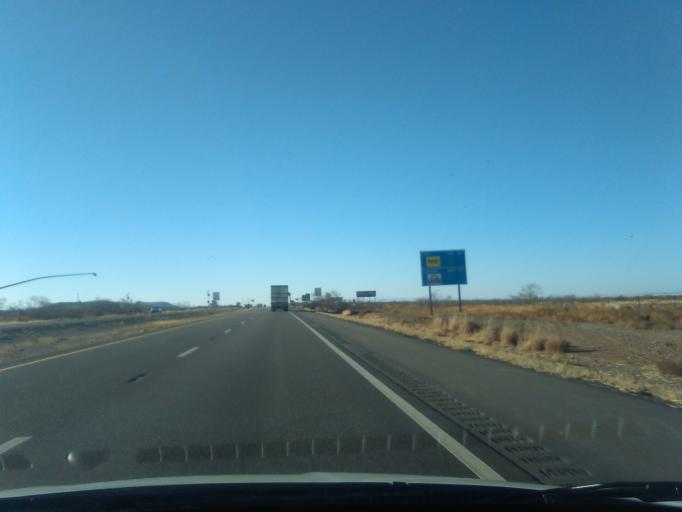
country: US
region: New Mexico
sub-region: Hidalgo County
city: Lordsburg
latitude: 32.3446
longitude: -108.7181
